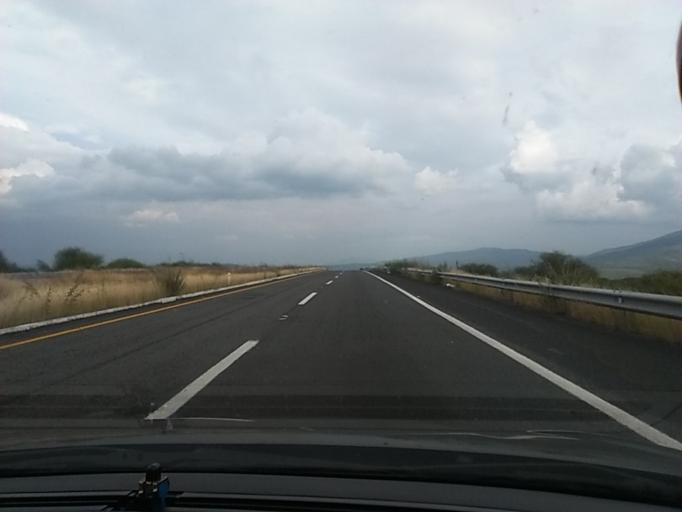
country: MX
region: Michoacan
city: Ecuandureo
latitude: 20.1793
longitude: -102.2679
